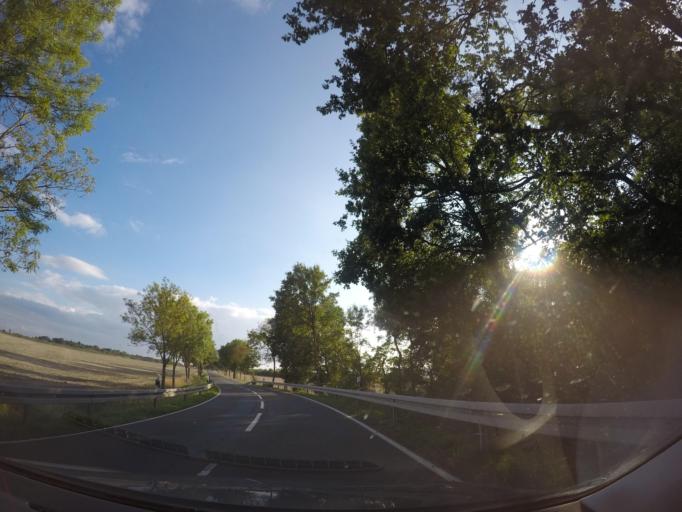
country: DE
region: Saxony-Anhalt
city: Weferlingen
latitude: 52.3563
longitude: 11.0791
